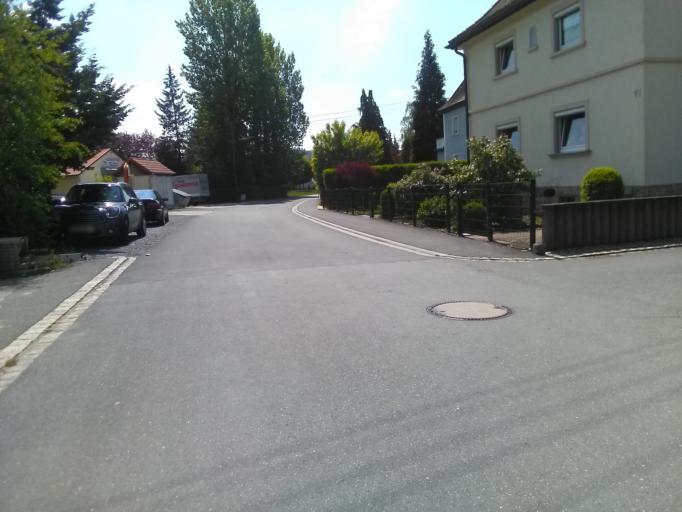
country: DE
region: Bavaria
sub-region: Upper Franconia
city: Kronach
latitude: 50.2165
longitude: 11.3066
